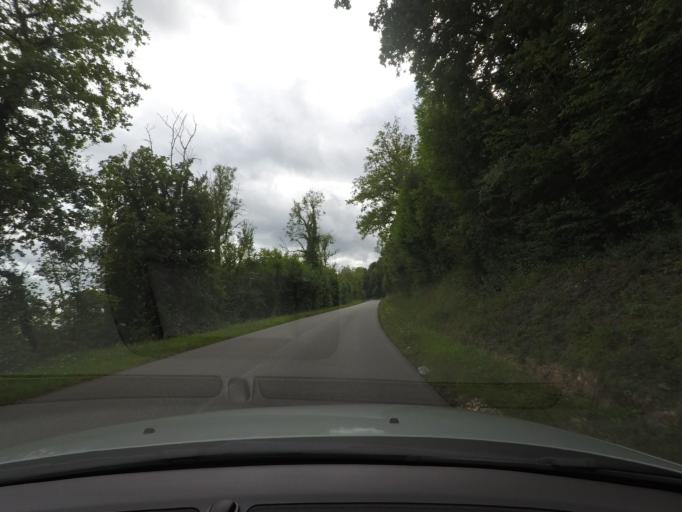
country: FR
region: Haute-Normandie
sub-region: Departement de l'Eure
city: Les Andelys
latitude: 49.2569
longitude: 1.3795
